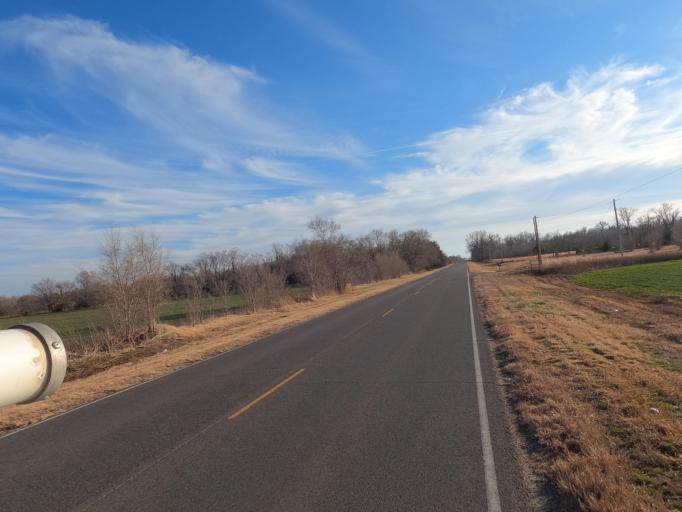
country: US
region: Kansas
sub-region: Reno County
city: Buhler
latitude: 38.1244
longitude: -97.7756
